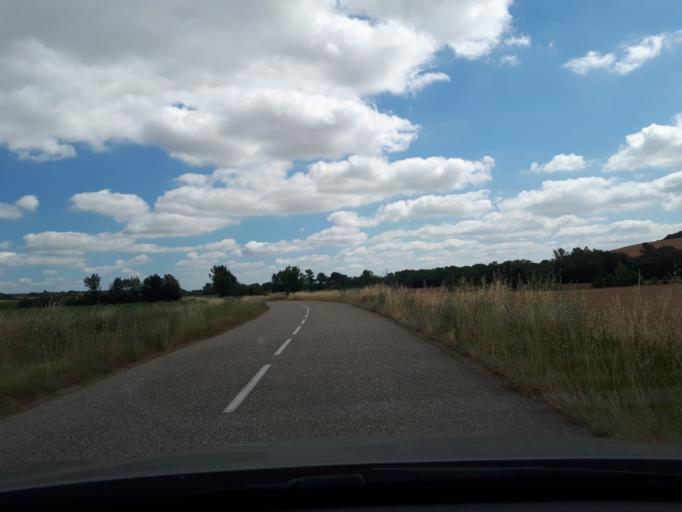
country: FR
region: Midi-Pyrenees
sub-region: Departement du Gers
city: Fleurance
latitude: 43.9476
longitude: 0.7601
